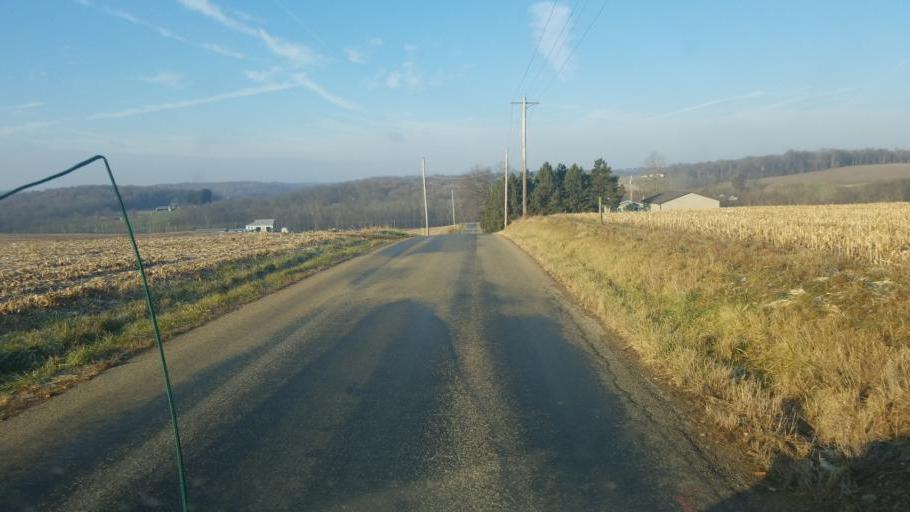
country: US
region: Ohio
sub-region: Knox County
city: Gambier
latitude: 40.4436
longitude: -82.3713
